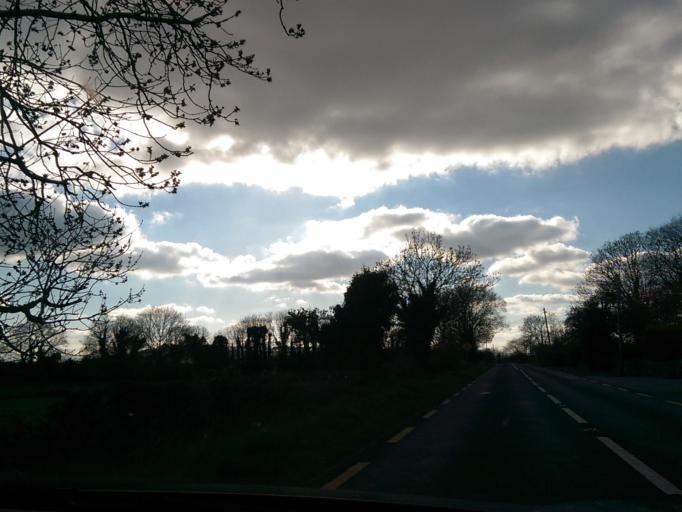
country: IE
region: Connaught
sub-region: County Galway
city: Loughrea
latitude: 53.2012
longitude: -8.4620
